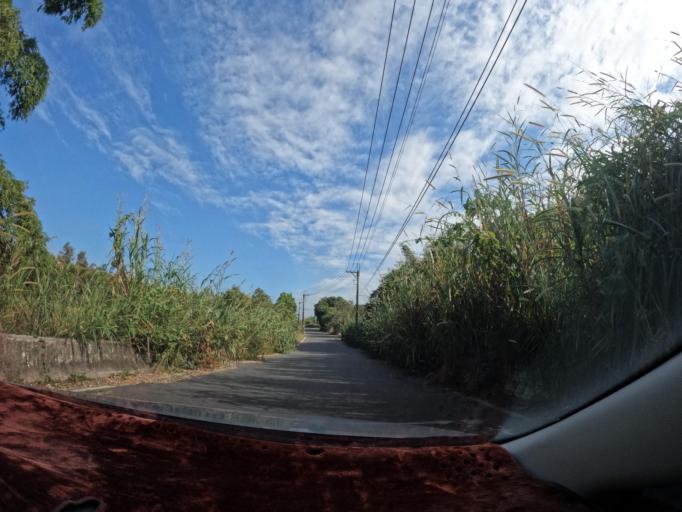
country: TW
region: Taiwan
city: Yujing
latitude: 23.0444
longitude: 120.3993
